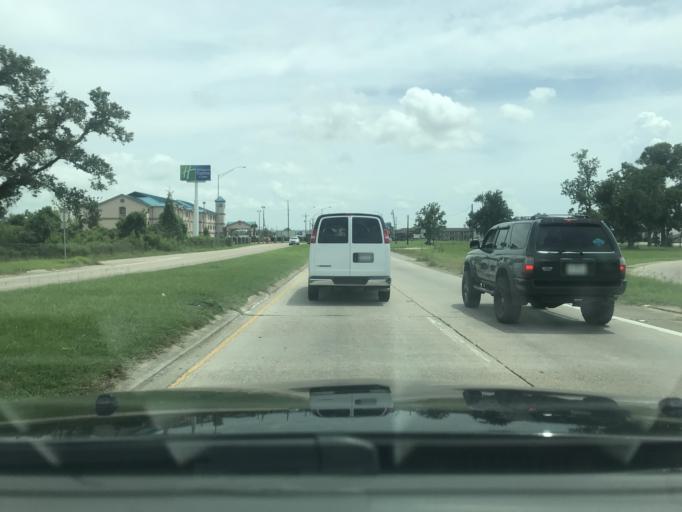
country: US
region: Louisiana
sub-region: Calcasieu Parish
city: Lake Charles
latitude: 30.2446
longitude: -93.1806
